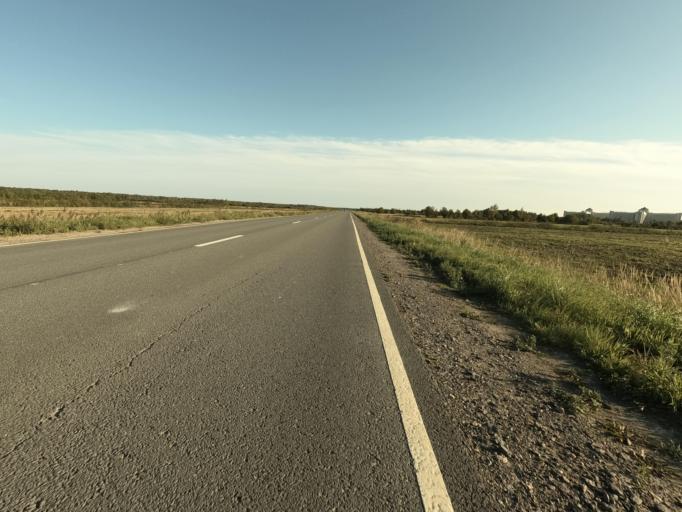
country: RU
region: St.-Petersburg
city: Sapernyy
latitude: 59.7518
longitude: 30.6364
